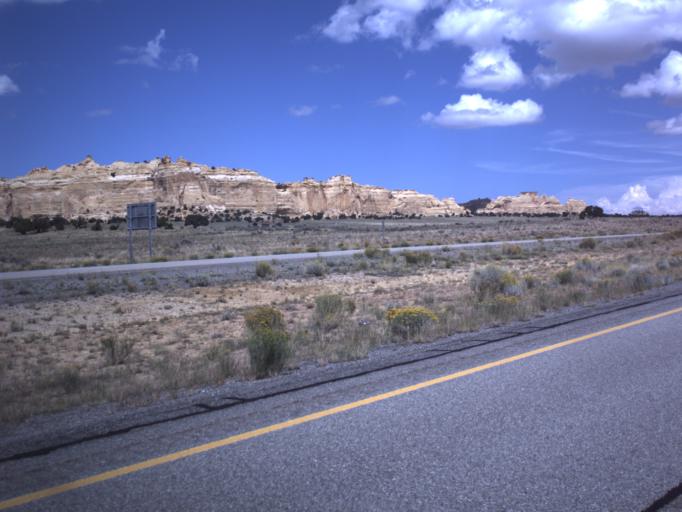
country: US
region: Utah
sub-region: Emery County
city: Castle Dale
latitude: 38.8691
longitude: -110.7742
